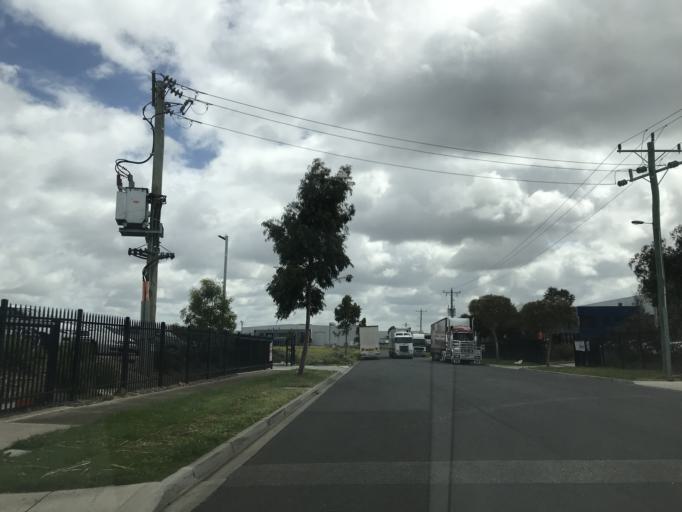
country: AU
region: Victoria
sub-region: Brimbank
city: Derrimut
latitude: -37.7905
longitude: 144.7793
